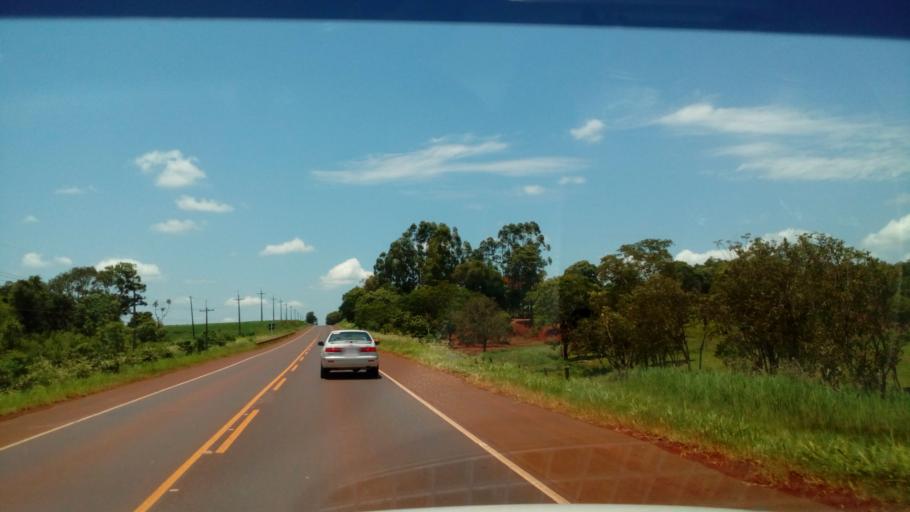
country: PY
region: Alto Parana
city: Naranjal
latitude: -25.9542
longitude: -55.1227
